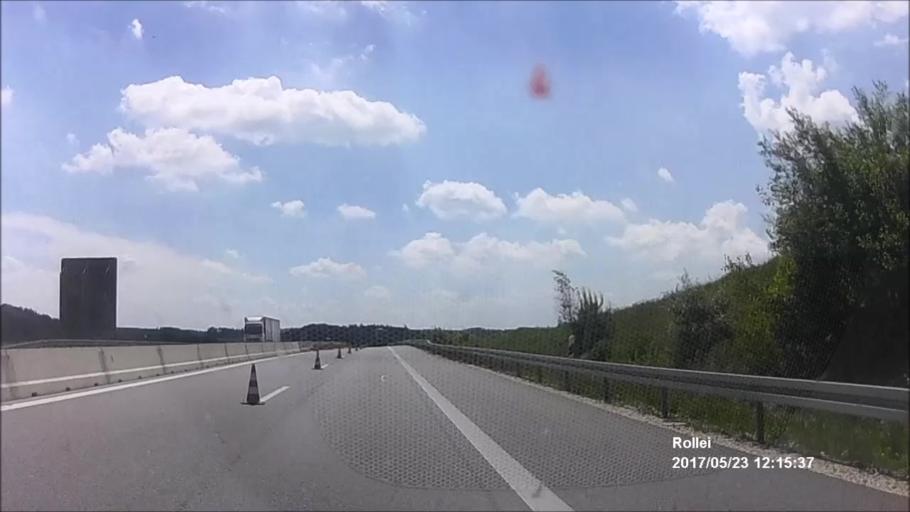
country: DE
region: Bavaria
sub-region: Upper Palatinate
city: Schierling
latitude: 48.8145
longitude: 12.1339
